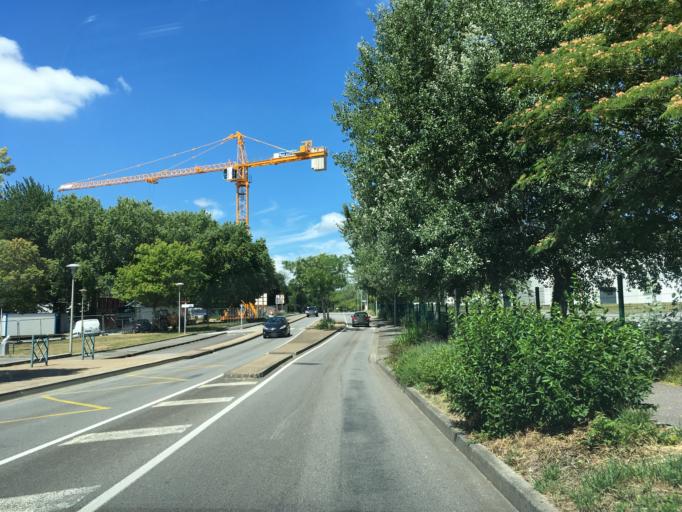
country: FR
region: Brittany
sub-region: Departement du Finistere
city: Quimper
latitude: 47.9715
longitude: -4.0945
